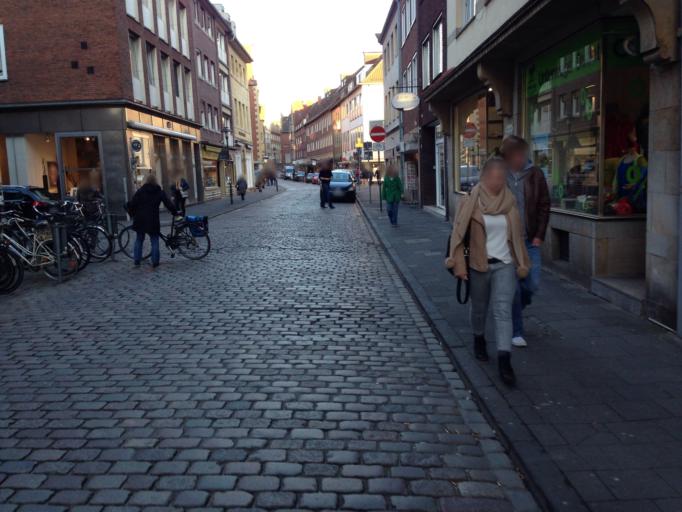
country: DE
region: North Rhine-Westphalia
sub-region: Regierungsbezirk Munster
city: Muenster
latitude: 51.9643
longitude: 7.6239
